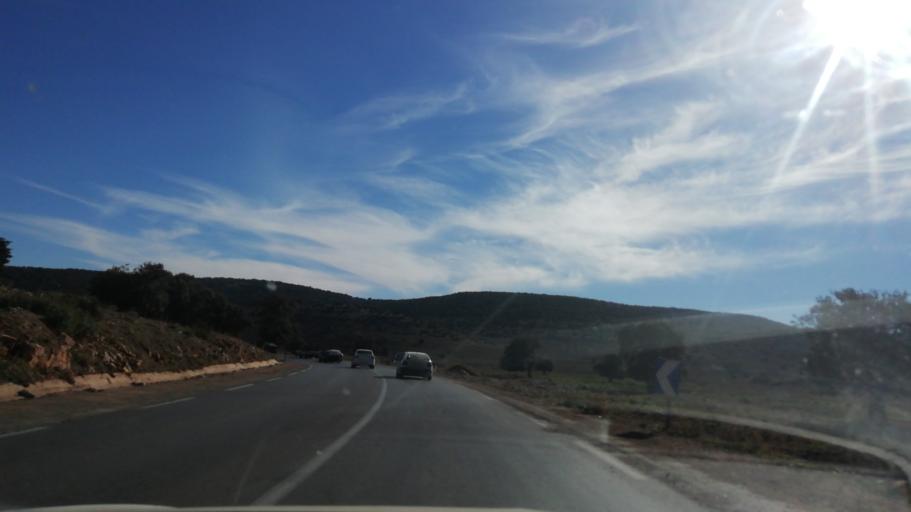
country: DZ
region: Tlemcen
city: Sebdou
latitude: 34.7212
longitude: -1.3391
